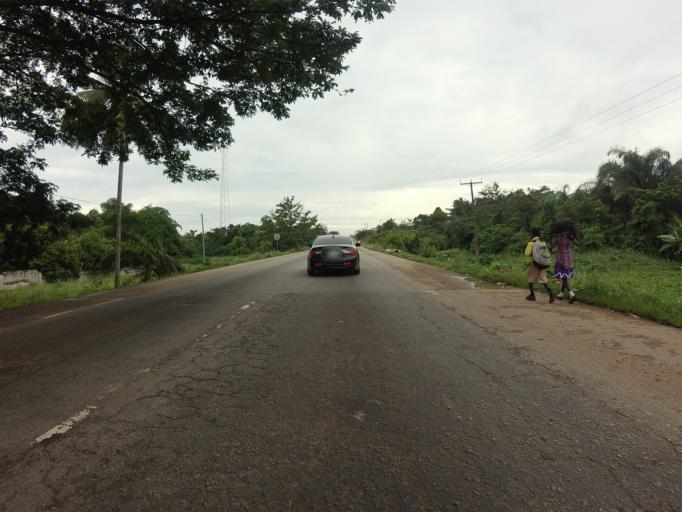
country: GH
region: Eastern
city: Nkawkaw
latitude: 6.4757
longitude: -0.6542
